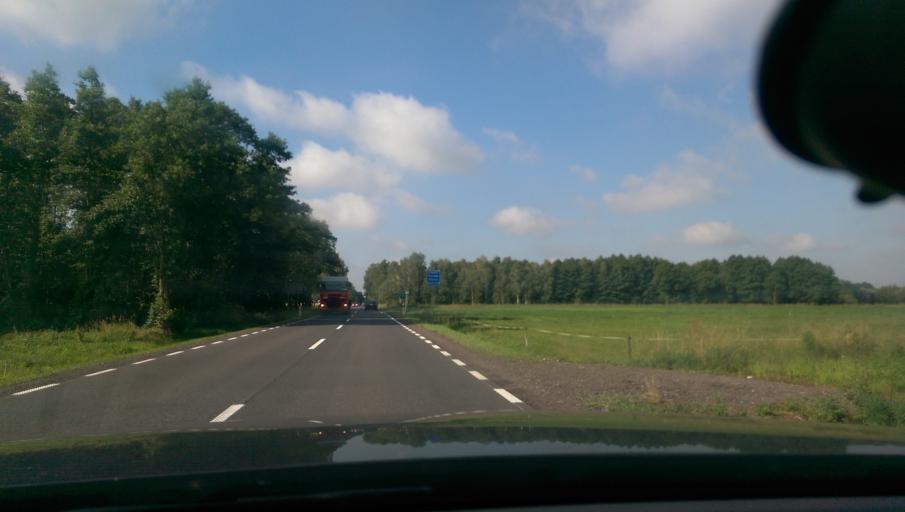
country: PL
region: Masovian Voivodeship
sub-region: Powiat plonski
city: Sochocin
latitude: 52.7180
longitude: 20.5023
